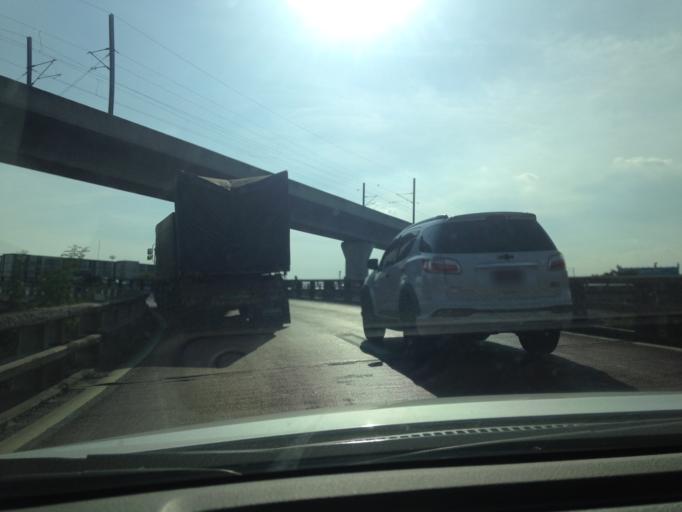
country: TH
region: Bangkok
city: Saphan Sung
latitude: 13.7321
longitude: 100.7014
